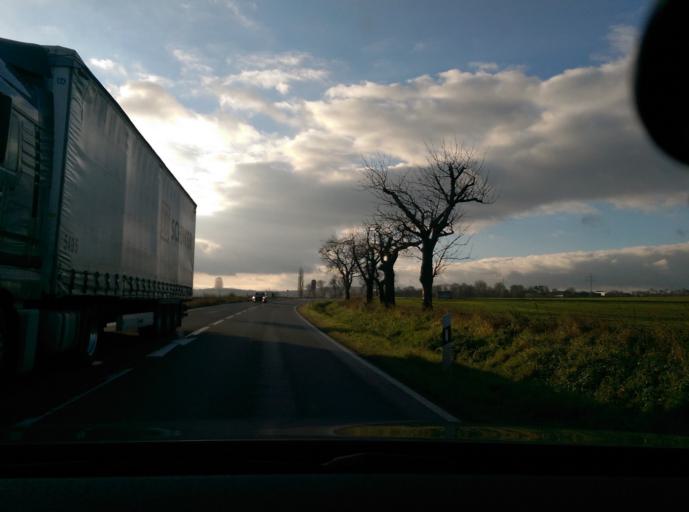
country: DE
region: Lower Saxony
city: Gemeinde Friedland
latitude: 51.3847
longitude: 9.9076
